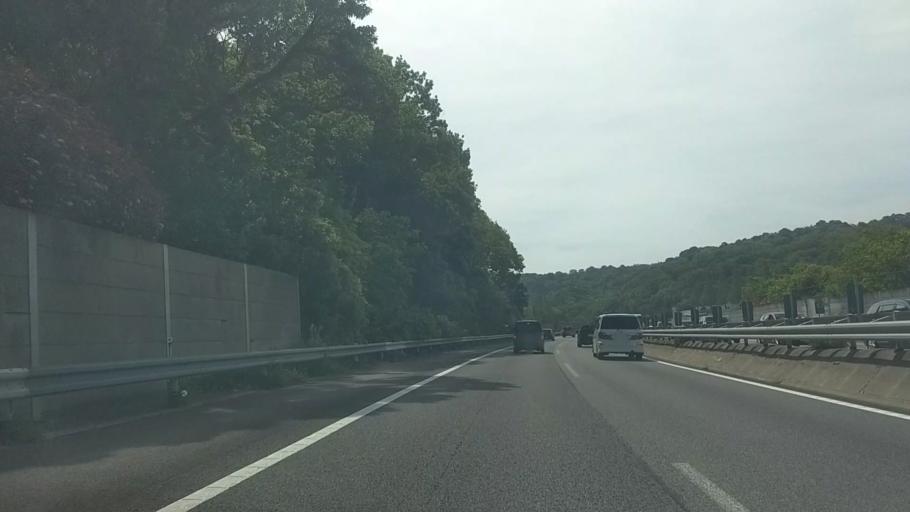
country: JP
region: Aichi
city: Okazaki
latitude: 34.9308
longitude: 137.2213
